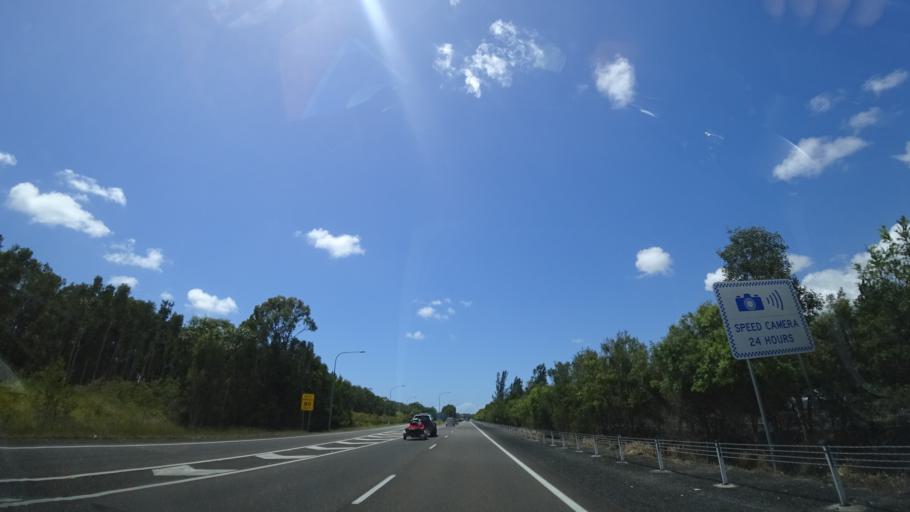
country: AU
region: Queensland
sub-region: Sunshine Coast
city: Mooloolaba
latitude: -26.6873
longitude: 153.1064
